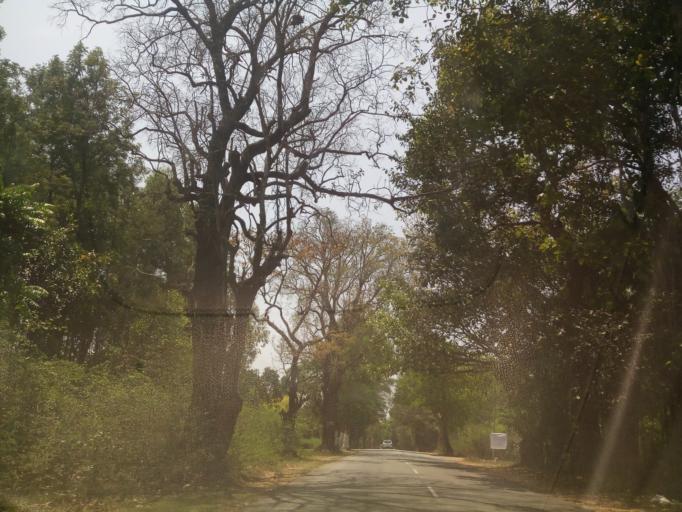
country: IN
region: Karnataka
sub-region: Hassan
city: Alur
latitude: 12.9522
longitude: 75.9074
